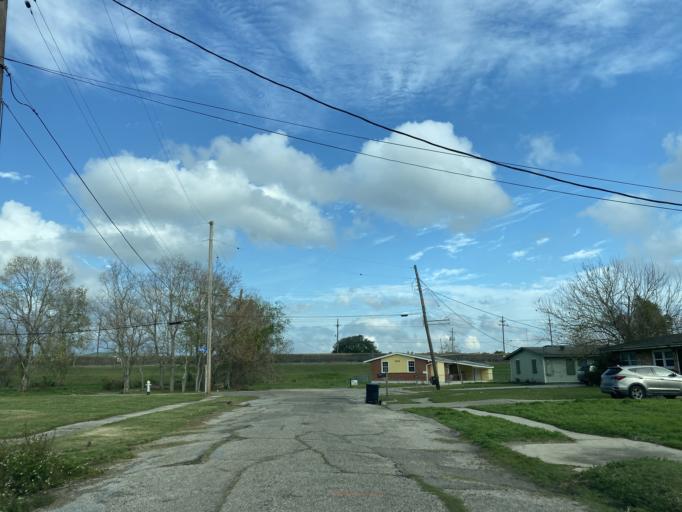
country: US
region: Louisiana
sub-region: Saint Bernard Parish
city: Arabi
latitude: 30.0243
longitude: -90.0366
